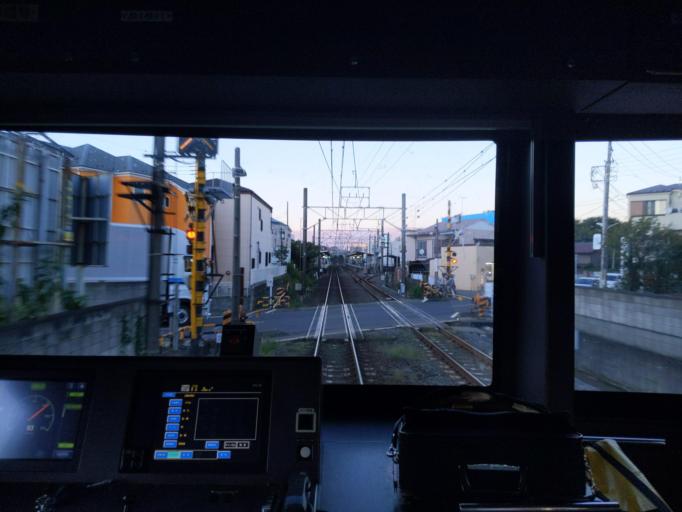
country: JP
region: Chiba
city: Funabashi
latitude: 35.7400
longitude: 139.9921
